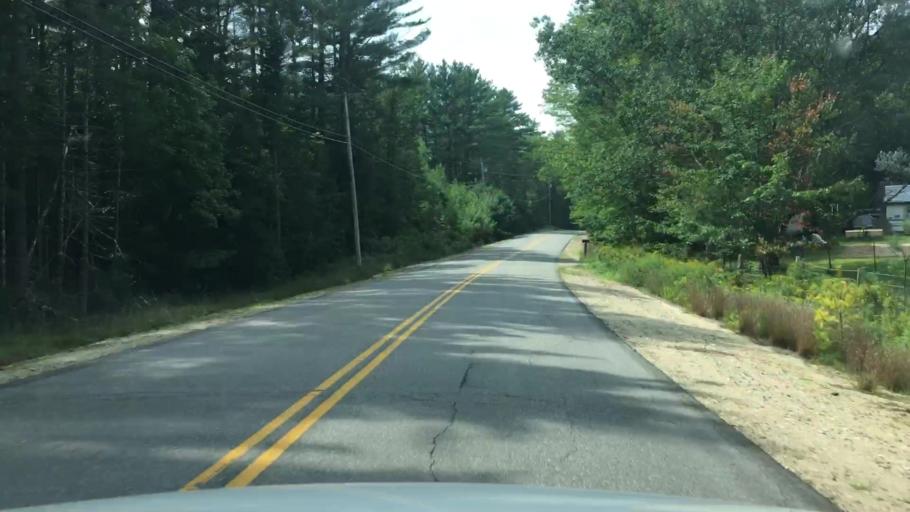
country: US
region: Maine
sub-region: Oxford County
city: Rumford
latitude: 44.5311
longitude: -70.6560
